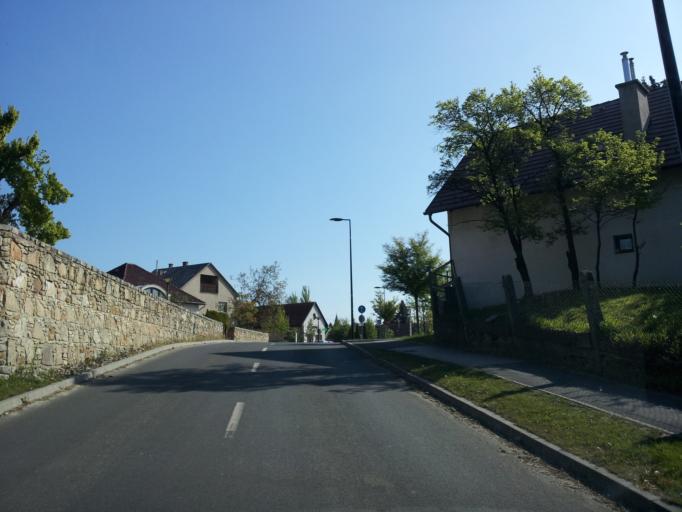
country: HU
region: Pest
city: Pilisszentivan
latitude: 47.5758
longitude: 18.8788
